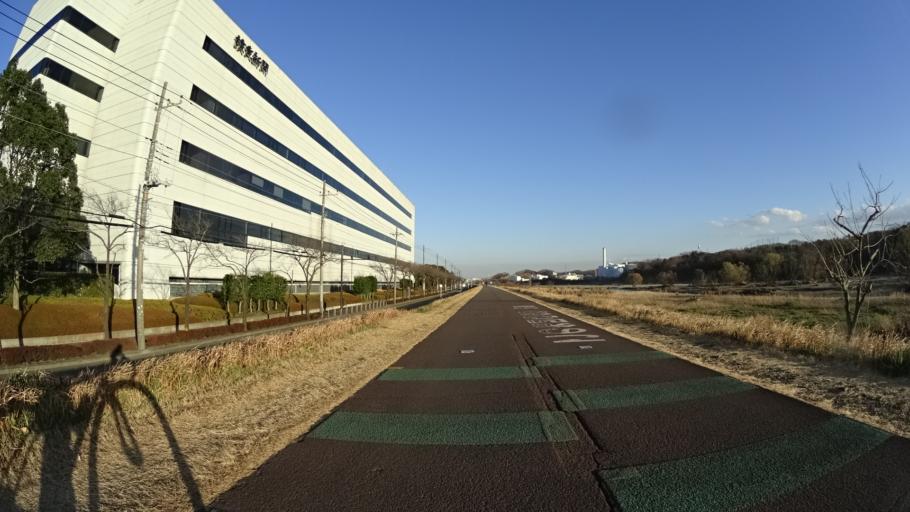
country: JP
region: Tokyo
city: Kokubunji
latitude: 35.6538
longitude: 139.4640
